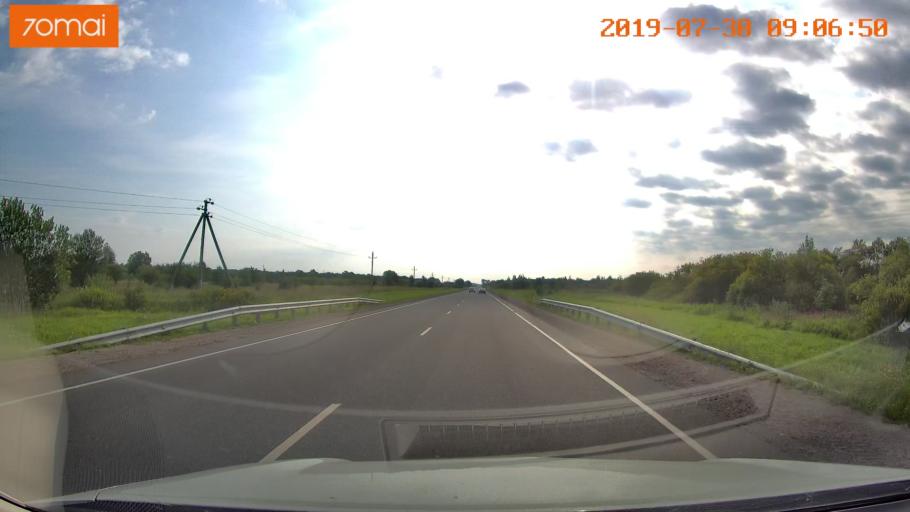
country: RU
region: Kaliningrad
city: Gusev
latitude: 54.6102
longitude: 22.3472
